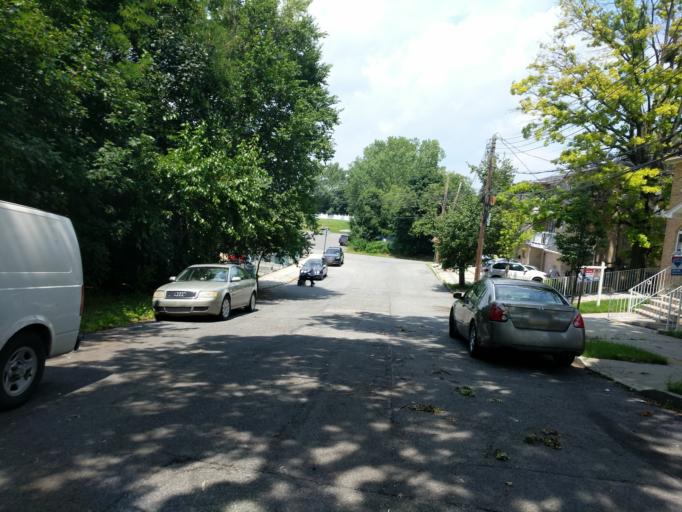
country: US
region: New York
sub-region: Bronx
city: The Bronx
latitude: 40.7933
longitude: -73.8425
